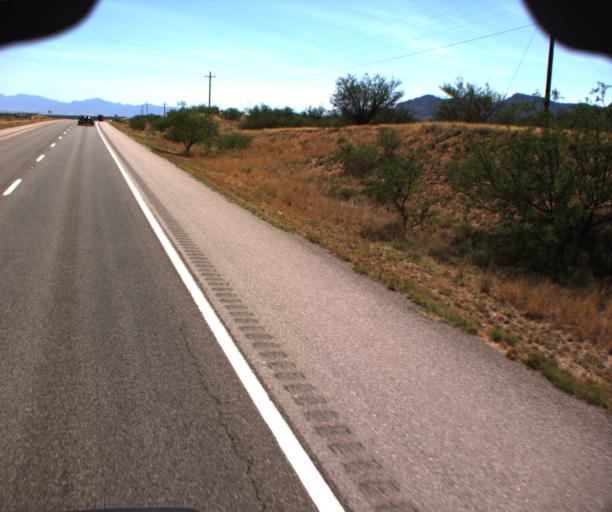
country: US
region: Arizona
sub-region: Cochise County
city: Whetstone
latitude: 31.8480
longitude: -110.3416
